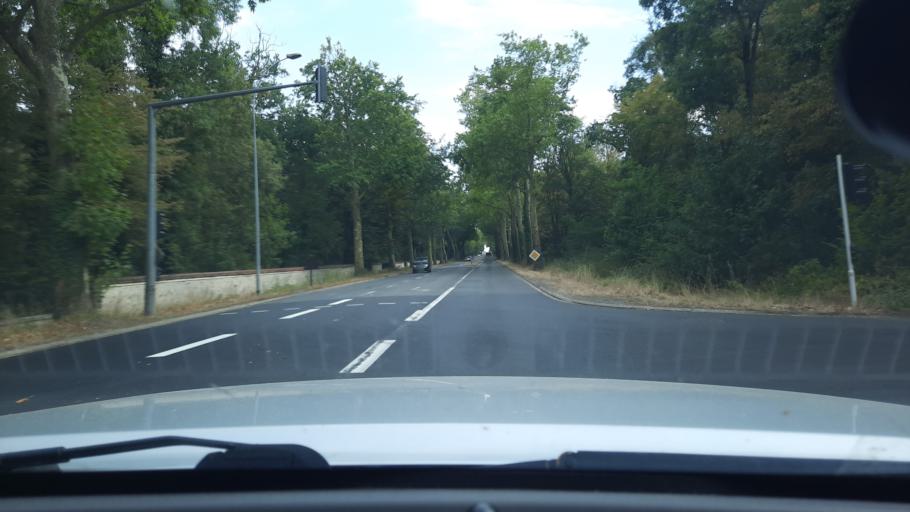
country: FR
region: Ile-de-France
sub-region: Departement de Seine-et-Marne
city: Dammarie-les-Lys
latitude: 48.5152
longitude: 2.6559
